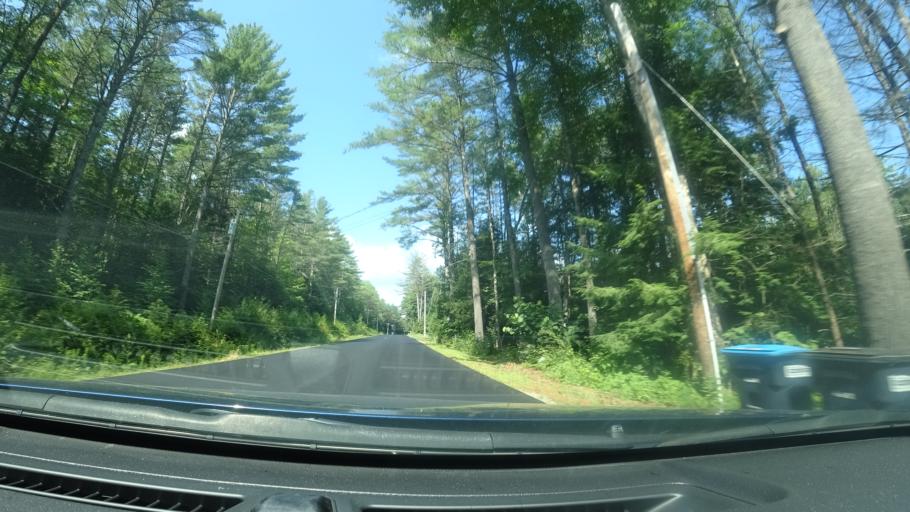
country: US
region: New York
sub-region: Warren County
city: Warrensburg
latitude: 43.6518
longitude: -73.8145
